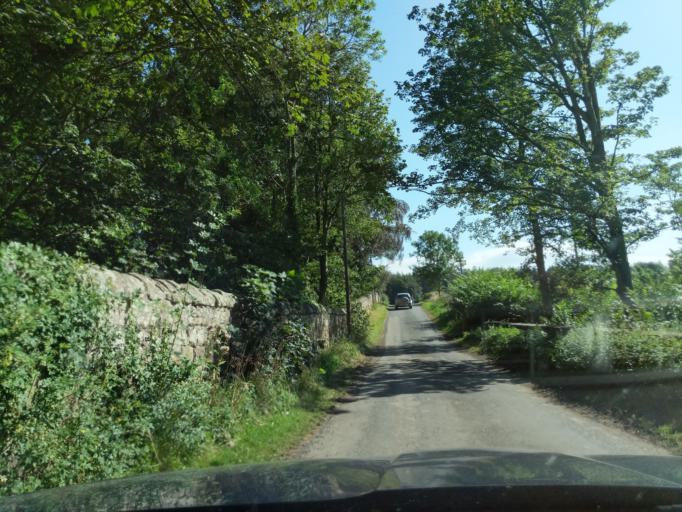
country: GB
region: Scotland
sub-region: The Scottish Borders
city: Coldstream
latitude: 55.6750
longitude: -2.1878
